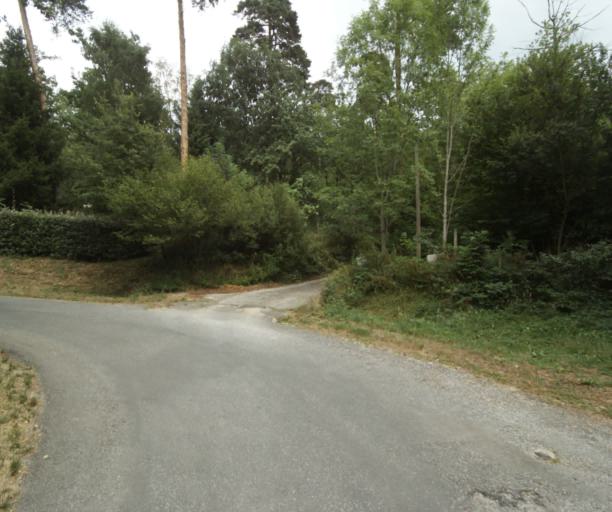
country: FR
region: Midi-Pyrenees
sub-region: Departement de la Haute-Garonne
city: Revel
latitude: 43.4306
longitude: 2.0339
